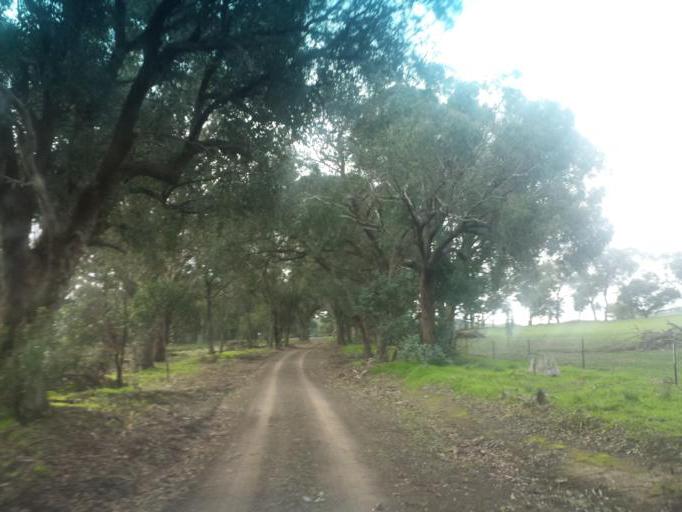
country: AU
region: Victoria
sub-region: Murrindindi
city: Kinglake West
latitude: -37.0156
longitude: 145.2502
